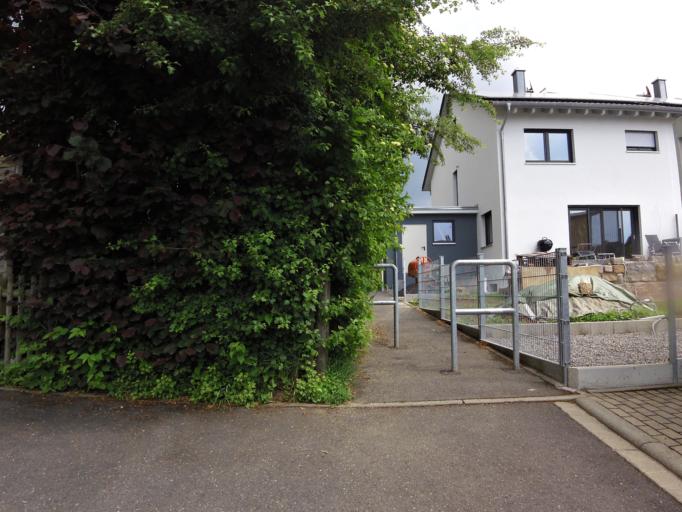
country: DE
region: Bavaria
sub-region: Regierungsbezirk Unterfranken
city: Waldbuttelbrunn
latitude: 49.7844
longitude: 9.8341
